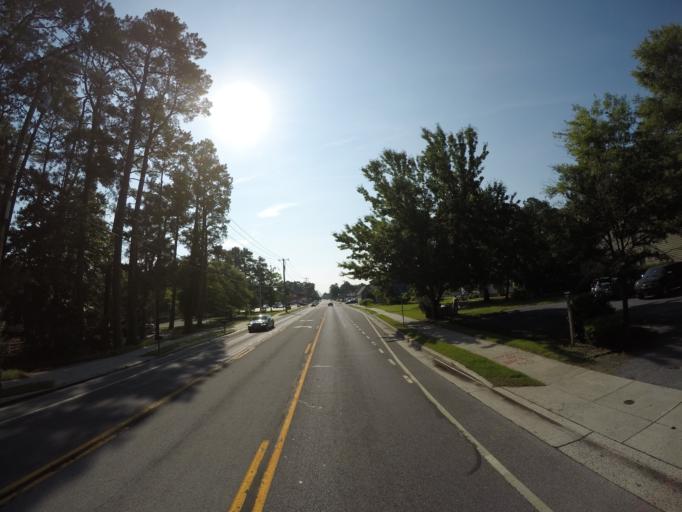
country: US
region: Delaware
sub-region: Sussex County
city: Ocean View
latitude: 38.5410
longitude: -75.0740
